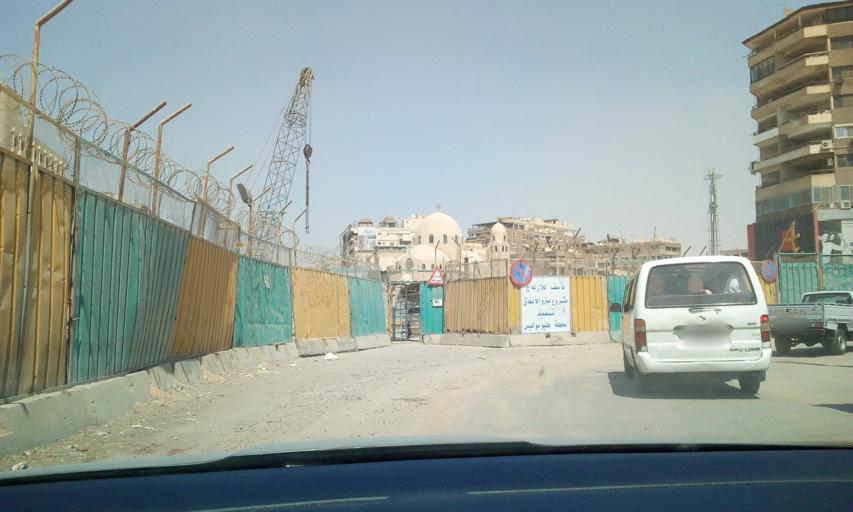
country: EG
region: Muhafazat al Qahirah
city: Cairo
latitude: 30.1077
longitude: 31.3377
